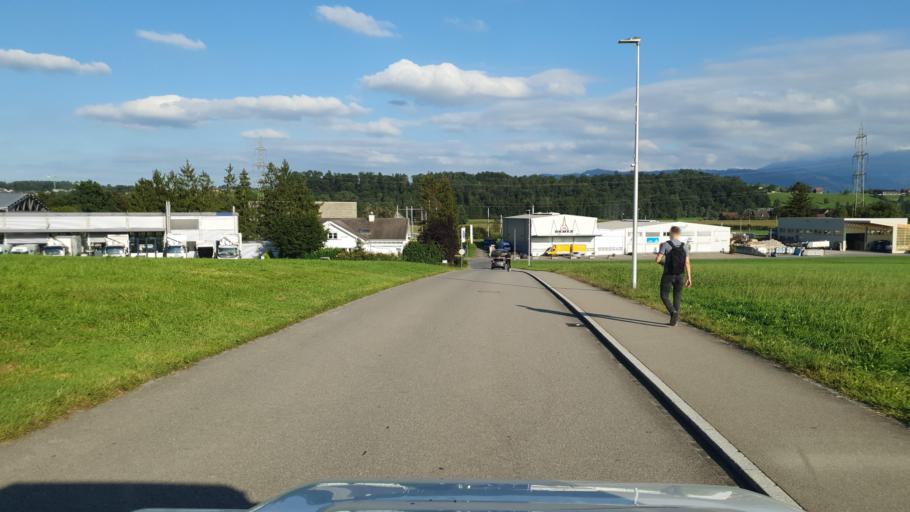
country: CH
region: Aargau
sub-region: Bezirk Muri
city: Oberruti
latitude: 47.1677
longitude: 8.4012
